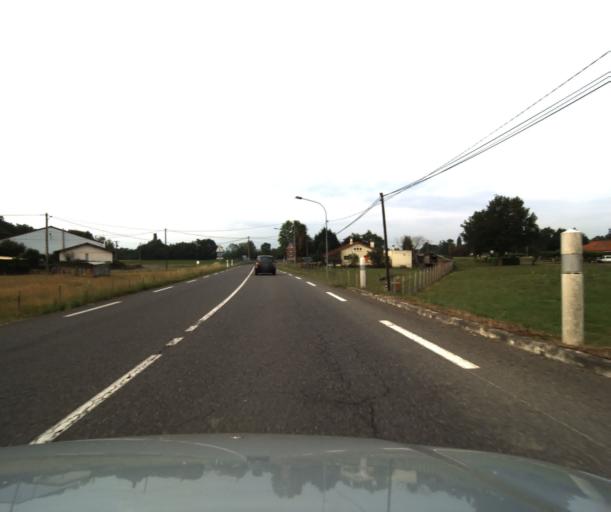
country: FR
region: Midi-Pyrenees
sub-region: Departement des Hautes-Pyrenees
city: Rabastens-de-Bigorre
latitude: 43.3906
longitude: 0.1611
